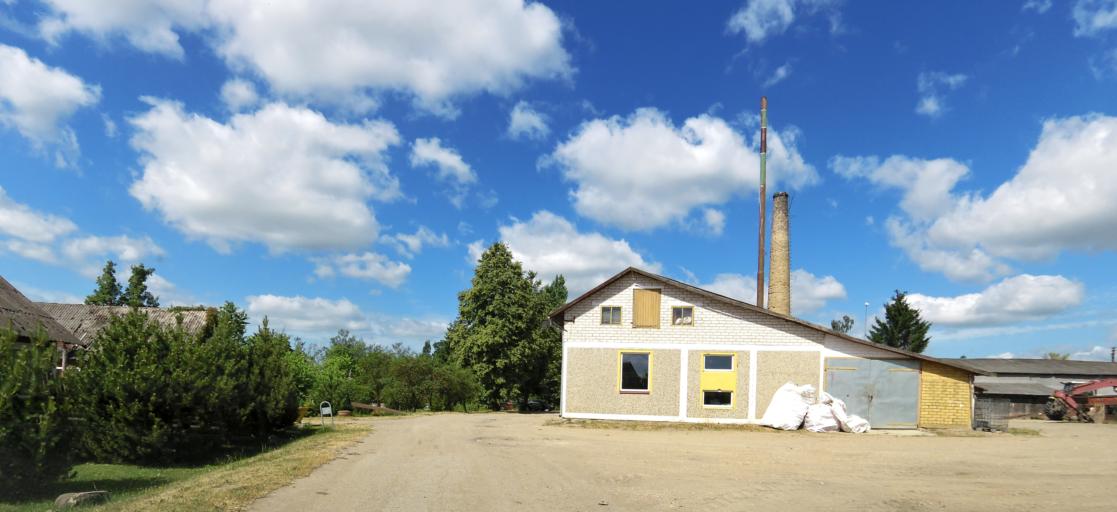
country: LT
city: Vabalninkas
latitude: 56.0220
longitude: 24.8069
